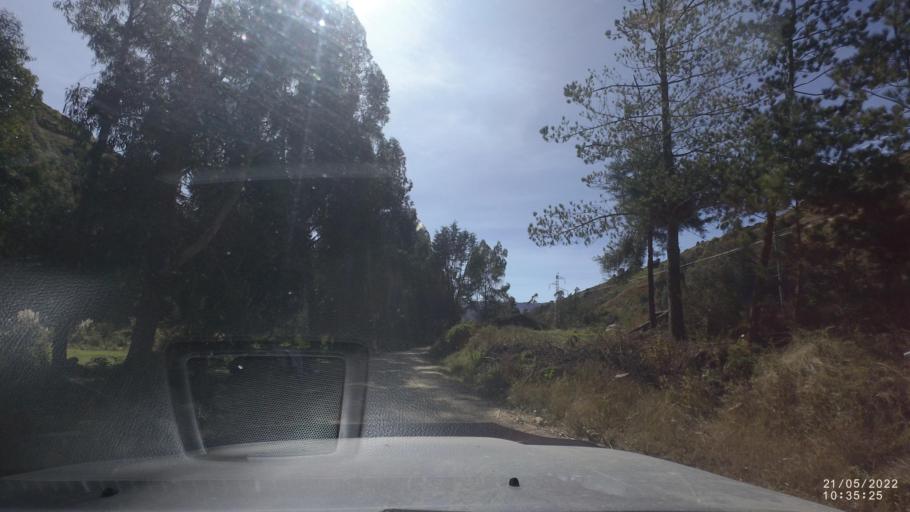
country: BO
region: Cochabamba
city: Colomi
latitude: -17.3179
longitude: -65.9277
